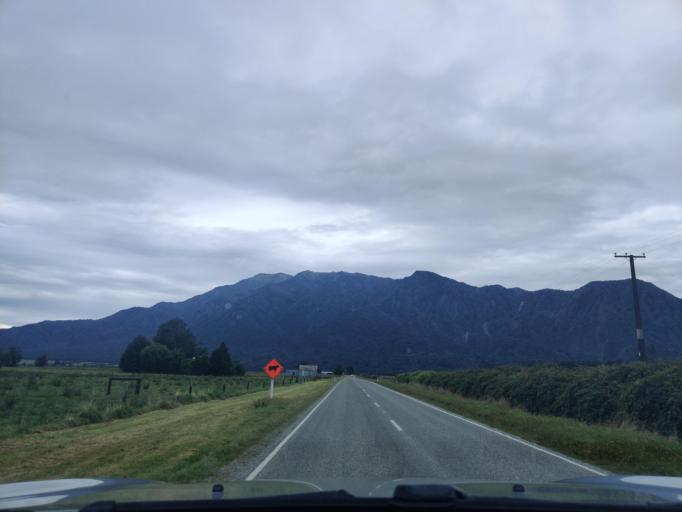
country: NZ
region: West Coast
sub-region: Westland District
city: Hokitika
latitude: -43.1534
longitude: 170.6020
